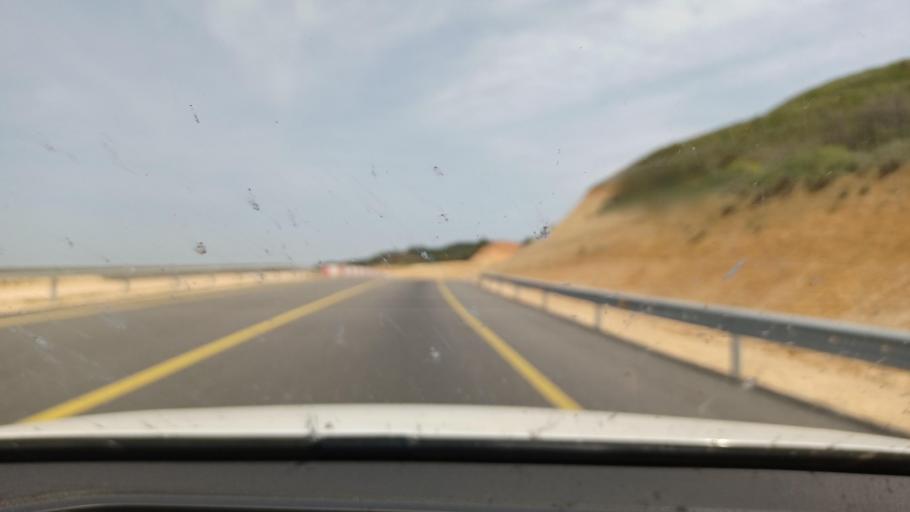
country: ES
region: Castille and Leon
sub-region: Provincia de Soria
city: San Esteban de Gormaz
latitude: 41.5798
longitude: -3.2023
